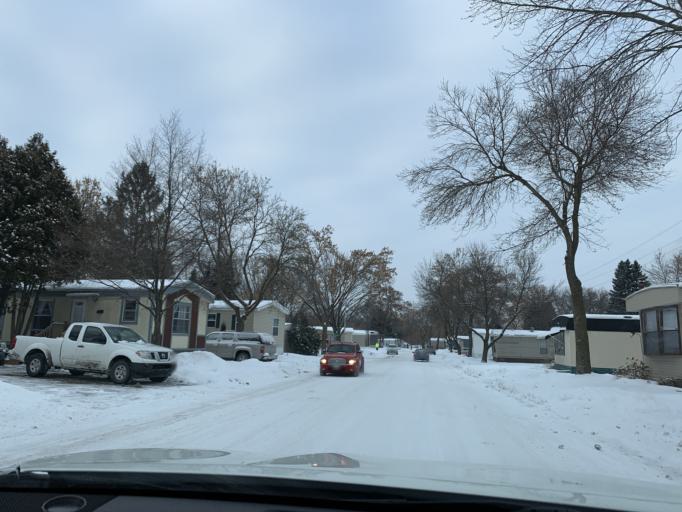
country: US
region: Minnesota
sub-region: Anoka County
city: Coon Rapids
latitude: 45.1572
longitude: -93.2953
